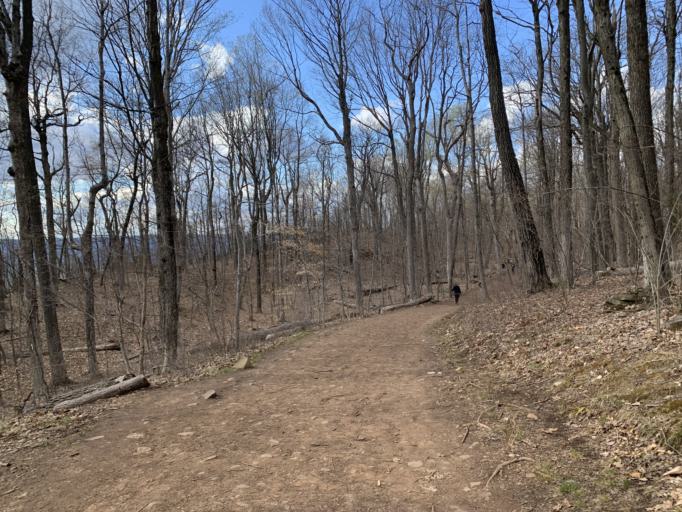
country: US
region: Connecticut
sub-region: Hartford County
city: Weatogue
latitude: 41.8310
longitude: -72.7983
